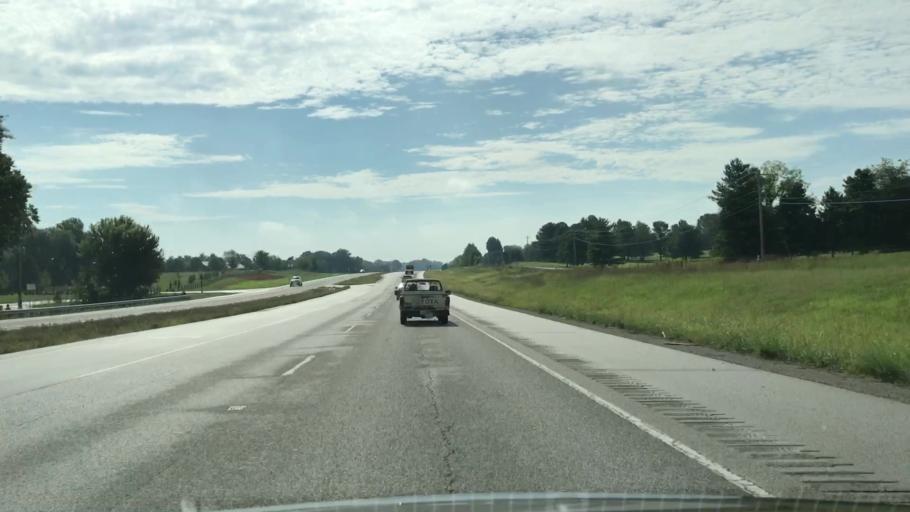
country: US
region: Kentucky
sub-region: Warren County
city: Plano
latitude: 36.8886
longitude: -86.3706
